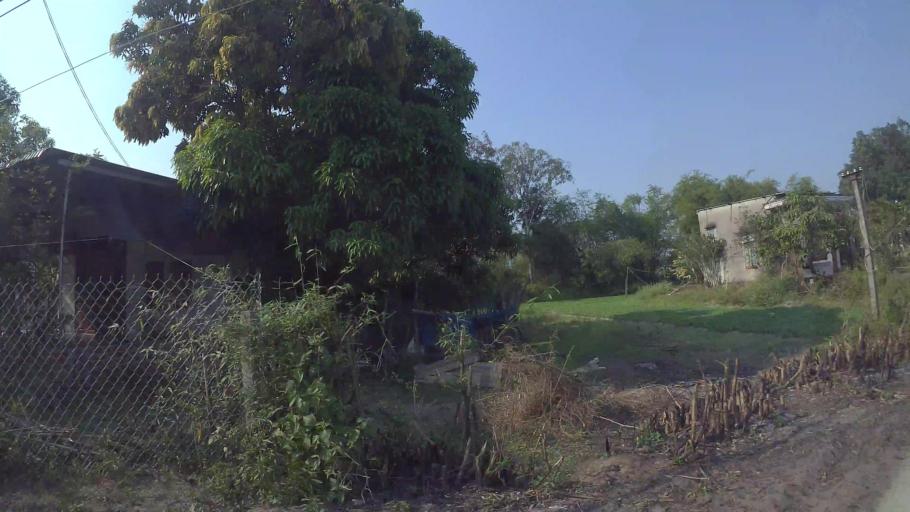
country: VN
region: Quang Nam
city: Quang Nam
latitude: 15.9487
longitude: 108.2572
